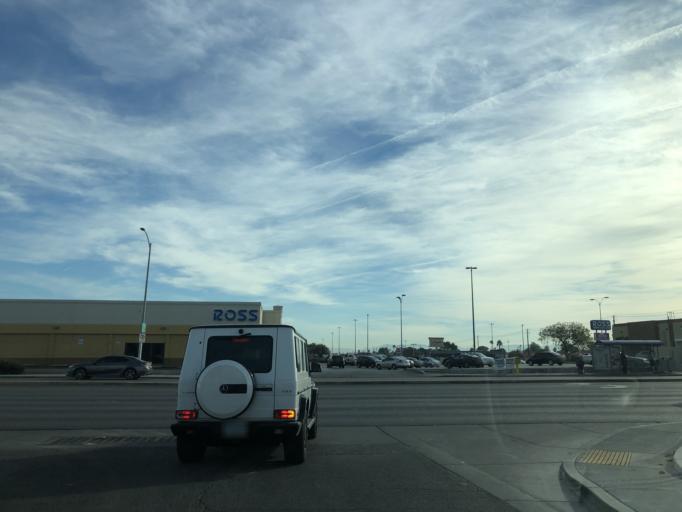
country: US
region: Nevada
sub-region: Clark County
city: Winchester
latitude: 36.1307
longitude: -115.1189
